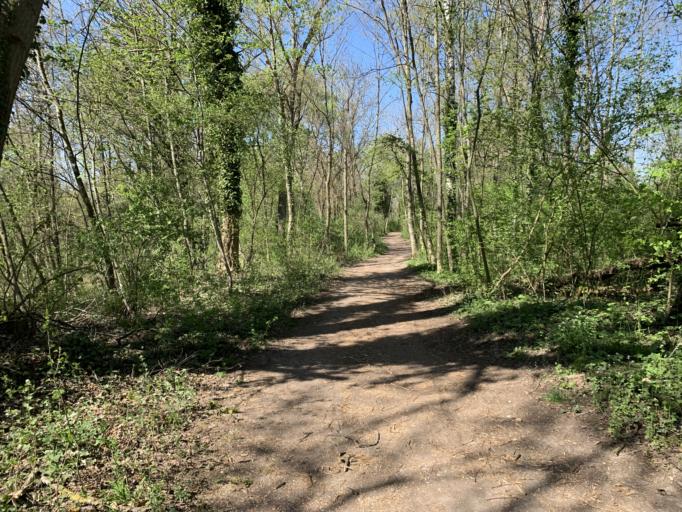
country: DE
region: Bavaria
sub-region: Swabia
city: Gersthofen
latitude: 48.4326
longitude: 10.8921
